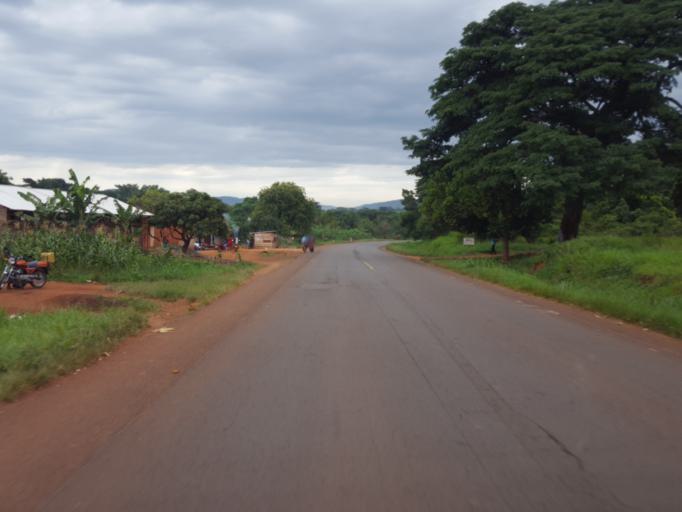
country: UG
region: Central Region
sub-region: Kiboga District
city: Kiboga
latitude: 0.8727
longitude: 31.8530
